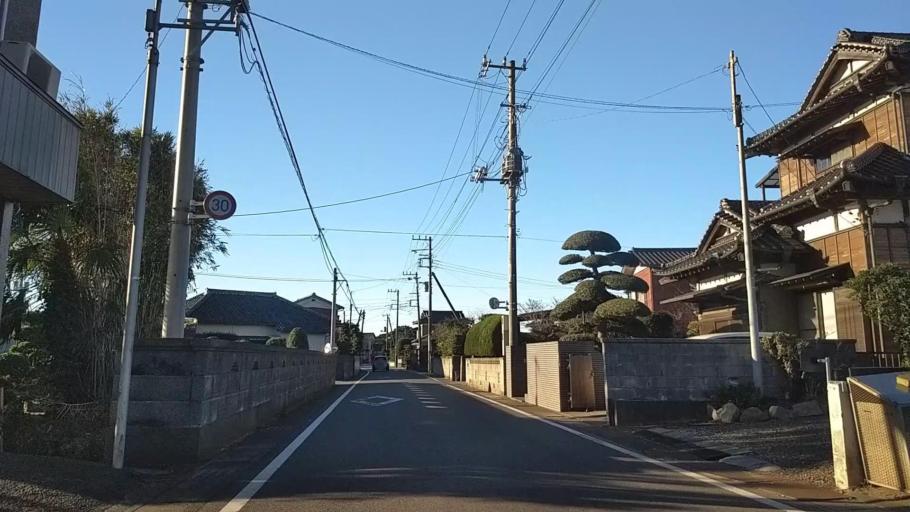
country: JP
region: Chiba
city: Kisarazu
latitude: 35.4294
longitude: 139.9227
